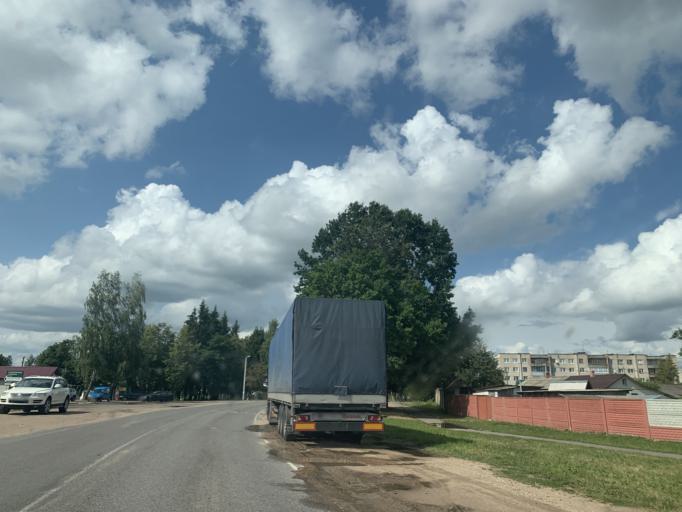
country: BY
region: Minsk
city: Enyerhyetykaw
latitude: 53.5846
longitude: 27.0528
